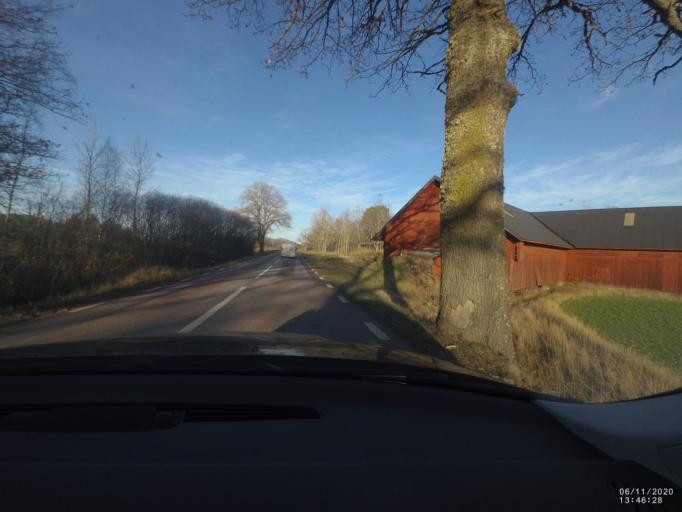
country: SE
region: Soedermanland
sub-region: Nykopings Kommun
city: Nykoping
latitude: 58.8871
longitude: 17.0894
